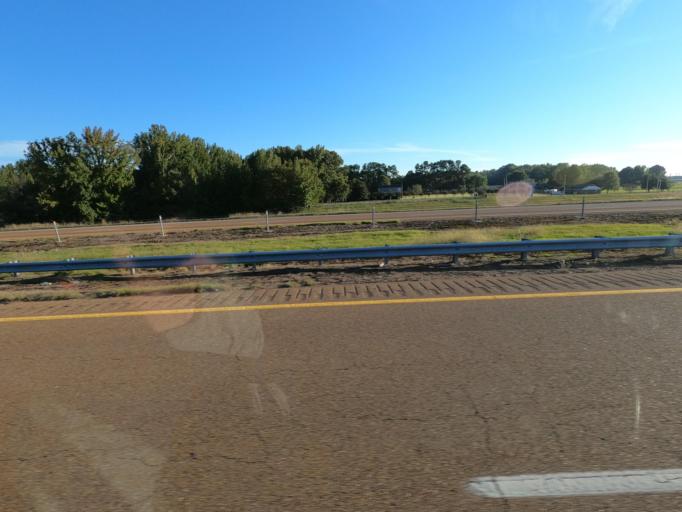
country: US
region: Tennessee
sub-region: Shelby County
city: Millington
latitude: 35.3084
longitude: -89.8217
